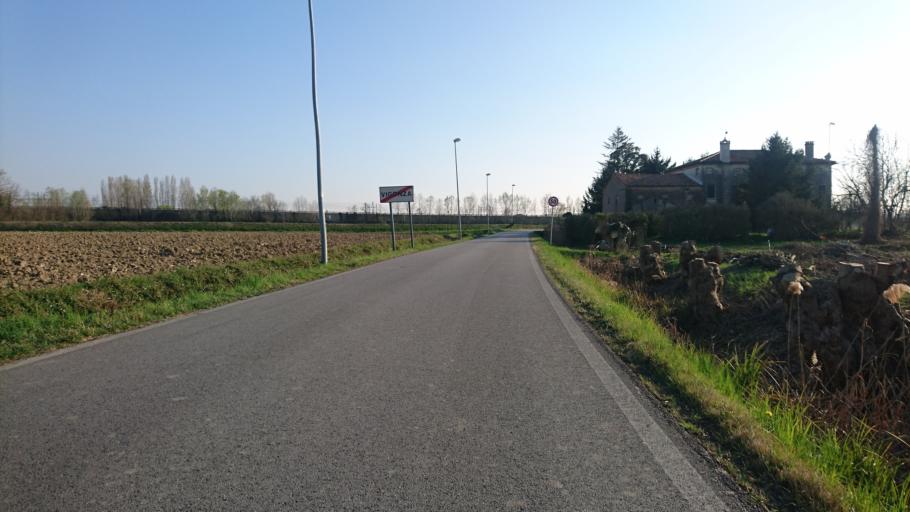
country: IT
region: Veneto
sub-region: Provincia di Padova
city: Vigonza
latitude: 45.4395
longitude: 11.9885
